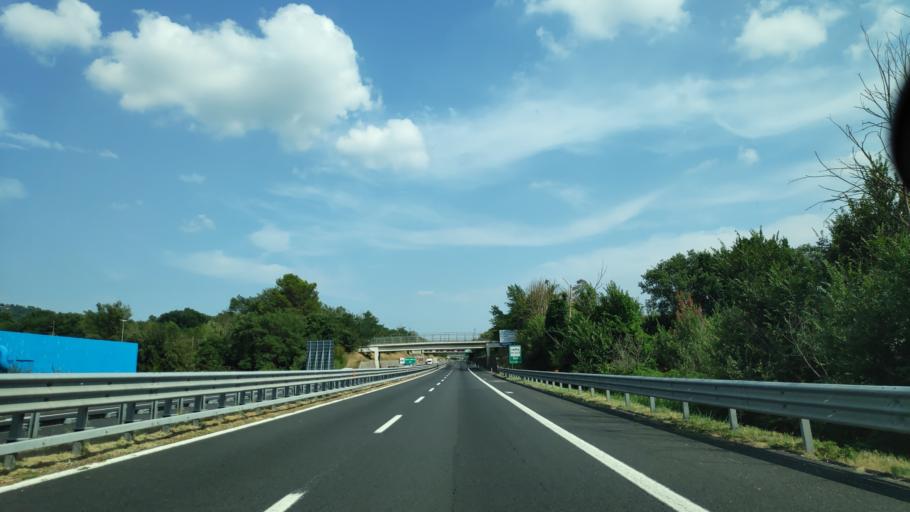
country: IT
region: Umbria
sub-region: Provincia di Terni
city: Attigliano
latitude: 42.5056
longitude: 12.3010
